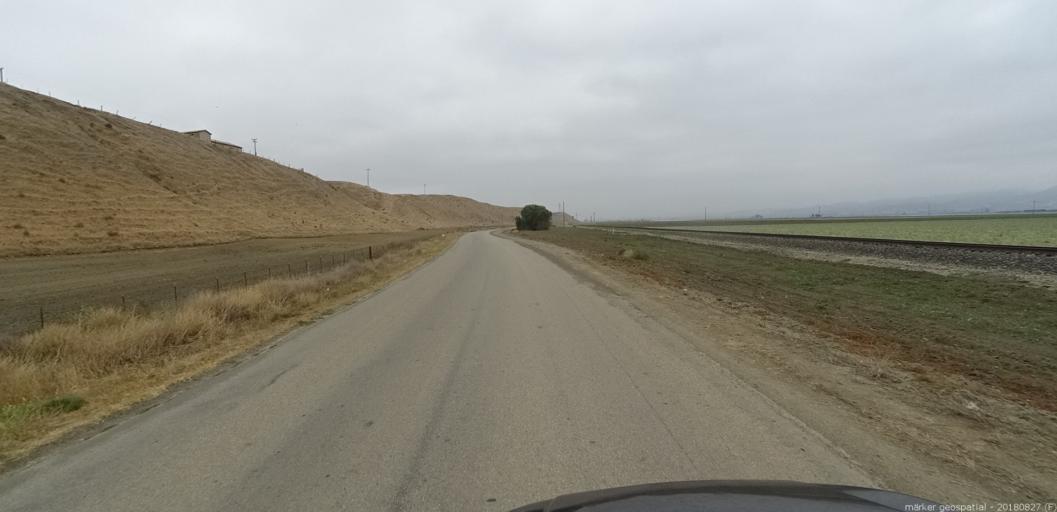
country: US
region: California
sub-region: Monterey County
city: King City
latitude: 36.2835
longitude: -121.1506
